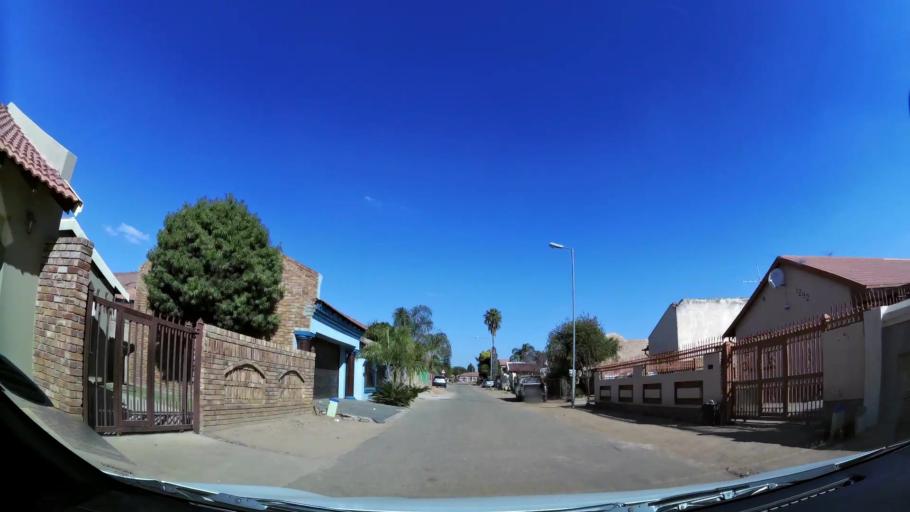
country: ZA
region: Gauteng
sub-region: City of Tshwane Metropolitan Municipality
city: Cullinan
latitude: -25.7147
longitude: 28.3912
